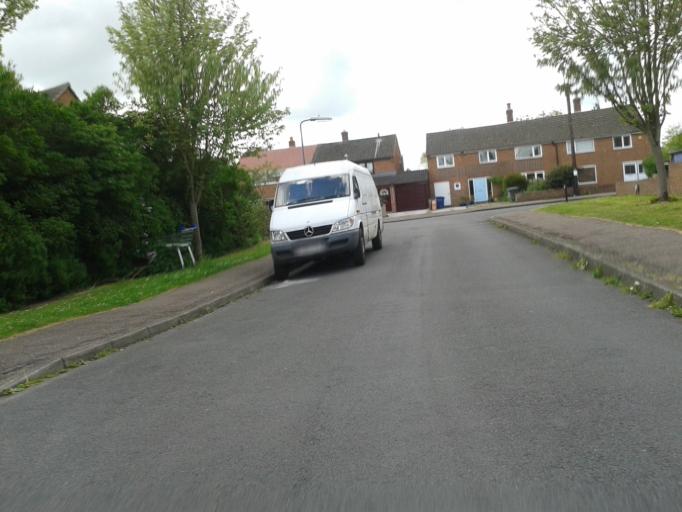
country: GB
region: England
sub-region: Cambridgeshire
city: Cambridge
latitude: 52.2212
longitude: 0.1557
